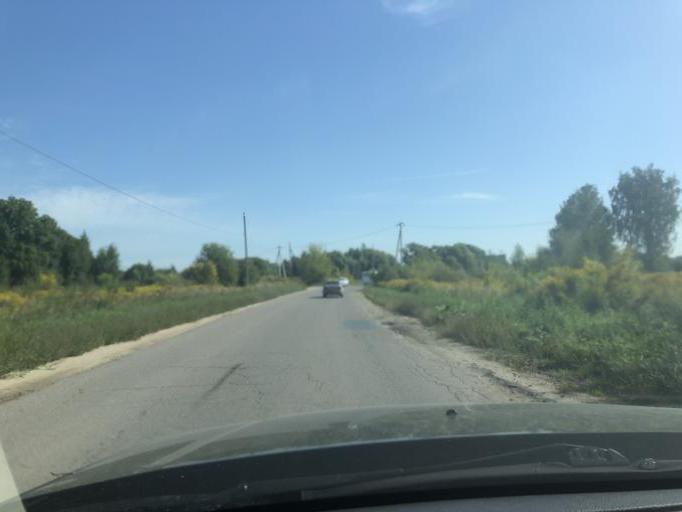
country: RU
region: Tula
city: Mendeleyevskiy
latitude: 54.1278
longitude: 37.6103
